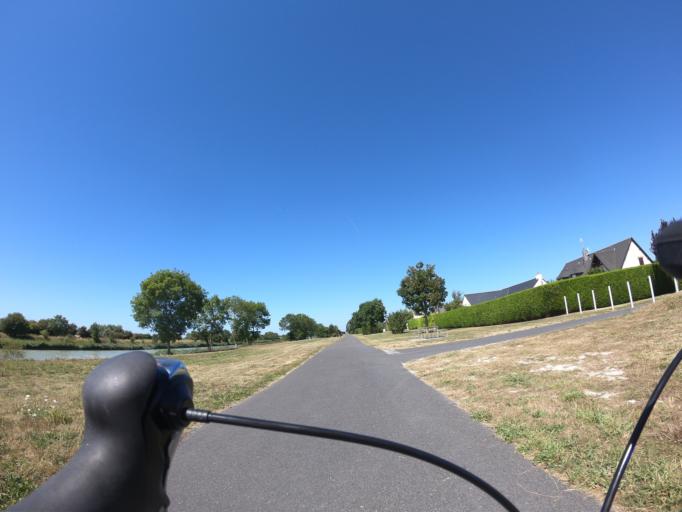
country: FR
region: Lower Normandy
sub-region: Departement de la Manche
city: Pontorson
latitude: 48.5931
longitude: -1.5147
